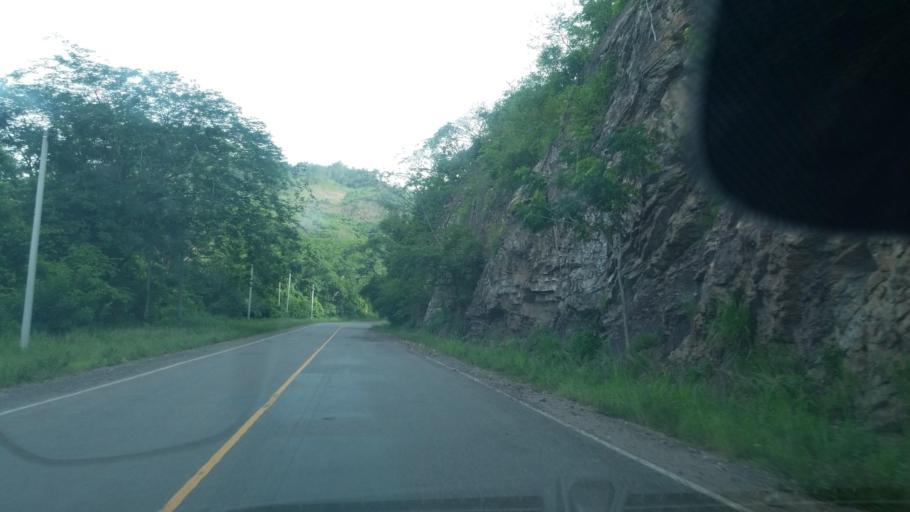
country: HN
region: Santa Barbara
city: Ilama
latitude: 15.0933
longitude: -88.2057
